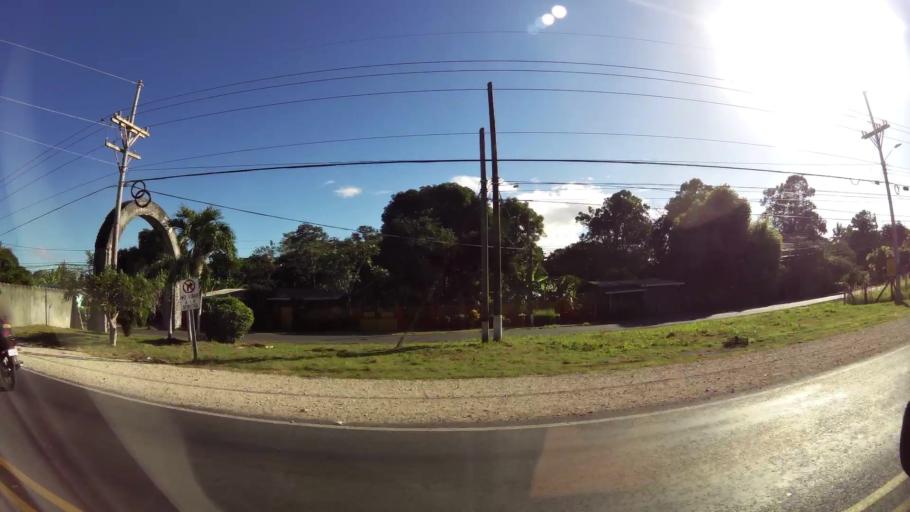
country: CR
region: Guanacaste
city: Belen
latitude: 10.4538
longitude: -85.5554
